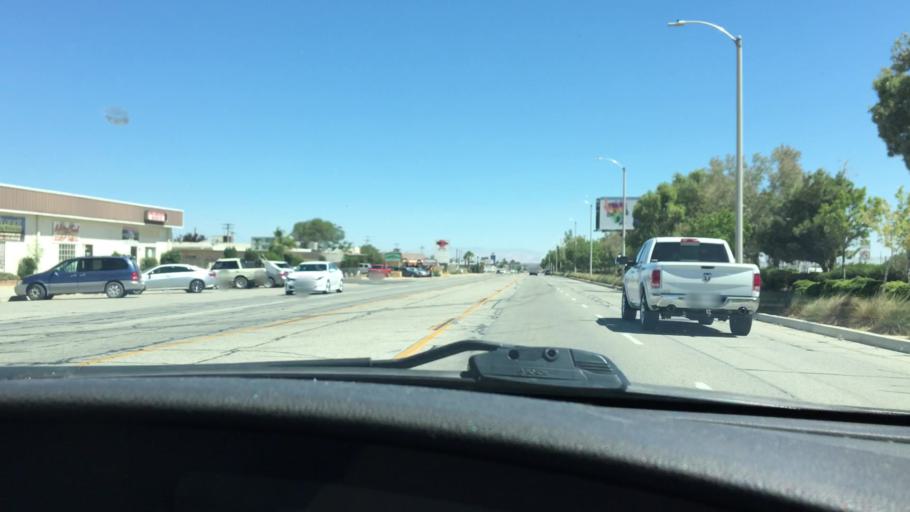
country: US
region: California
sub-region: Los Angeles County
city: Lancaster
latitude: 34.6496
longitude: -118.1289
